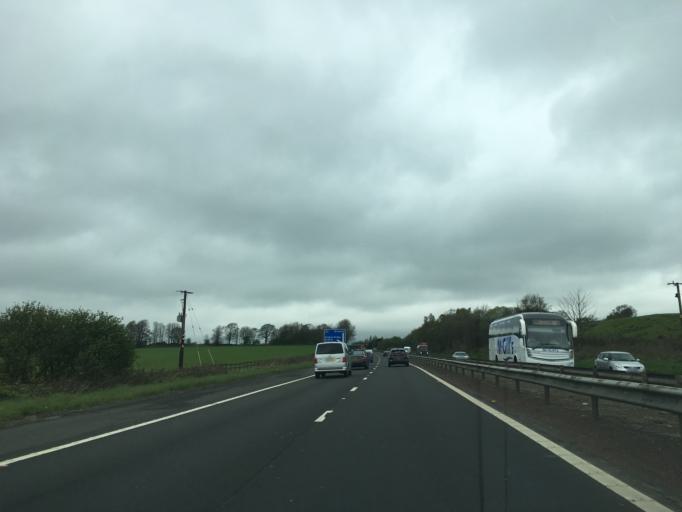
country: GB
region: Scotland
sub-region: Renfrewshire
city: Bishopton
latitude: 55.8952
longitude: -4.4821
